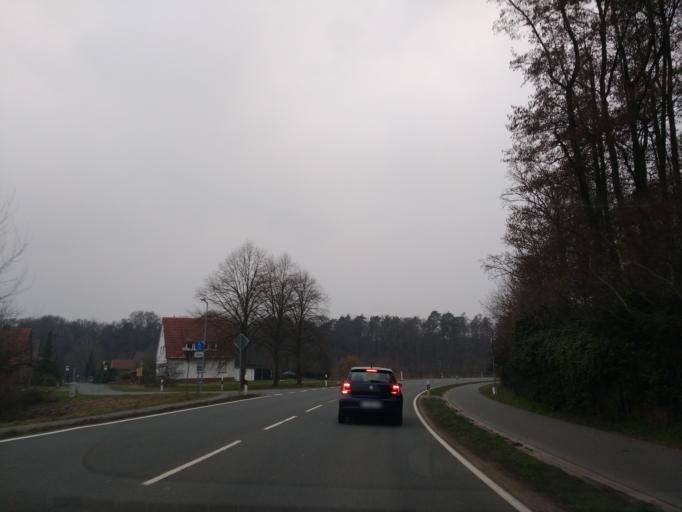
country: DE
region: North Rhine-Westphalia
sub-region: Regierungsbezirk Munster
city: Lotte
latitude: 52.2978
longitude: 7.9230
